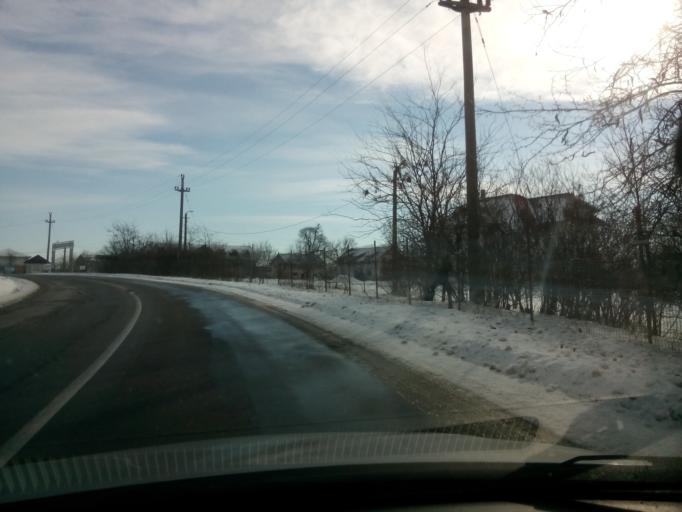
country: RO
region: Calarasi
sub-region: Comuna Soldanu
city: Negoesti
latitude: 44.2315
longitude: 26.4889
